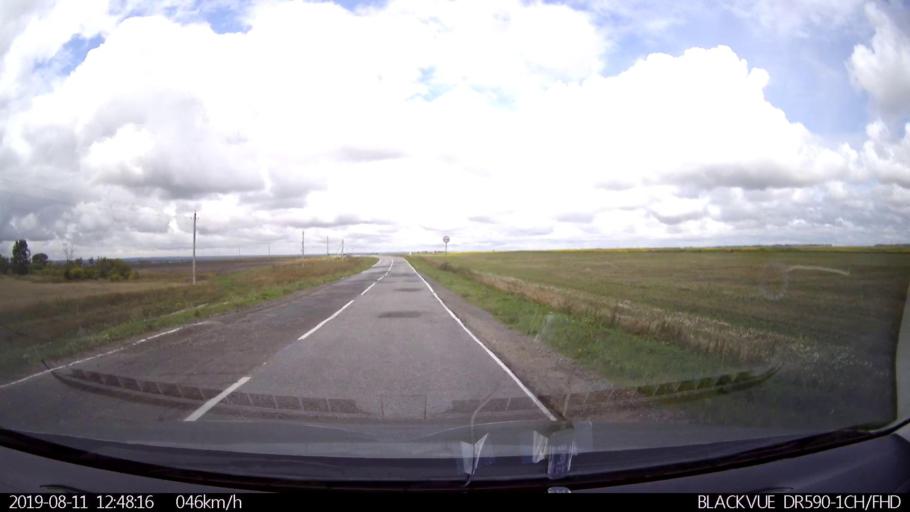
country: RU
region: Ulyanovsk
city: Ignatovka
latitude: 53.8731
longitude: 47.7008
